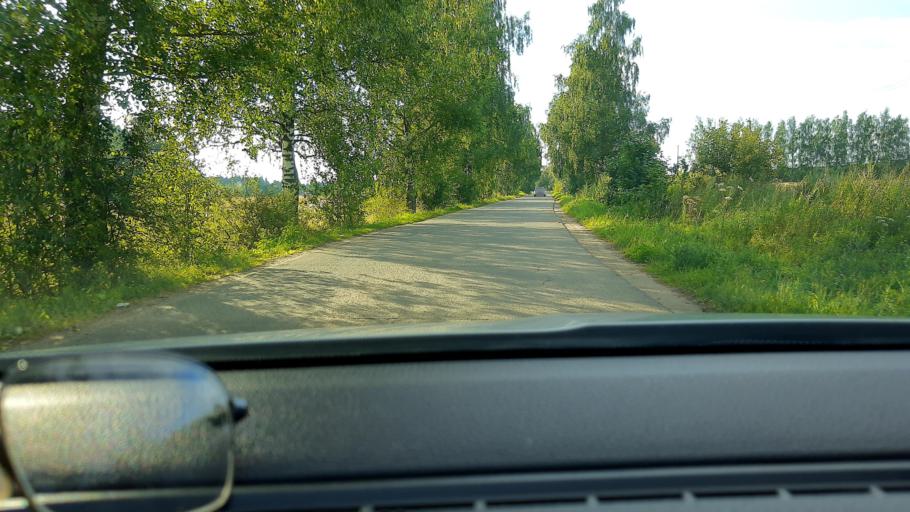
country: RU
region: Moskovskaya
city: Nekrasovskiy
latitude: 56.0977
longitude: 37.5347
